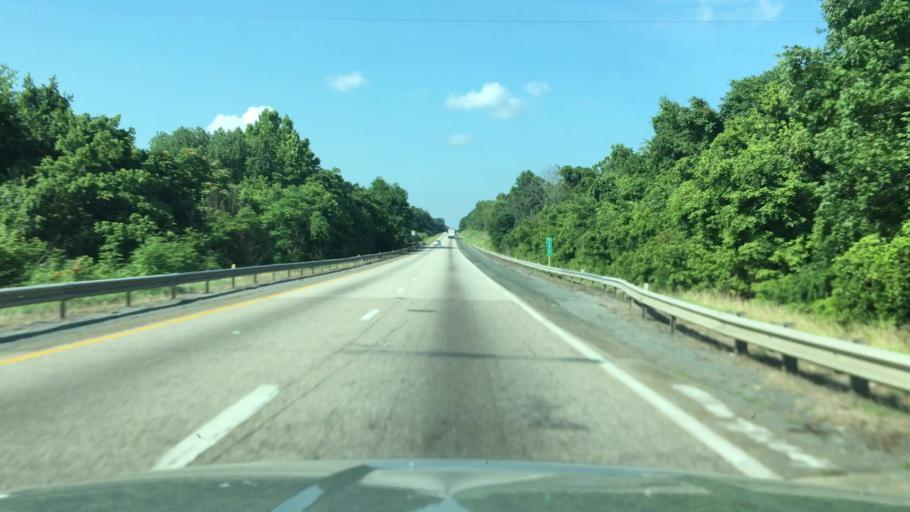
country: US
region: Virginia
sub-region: Rockbridge County
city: Glasgow
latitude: 37.6407
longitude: -79.5612
